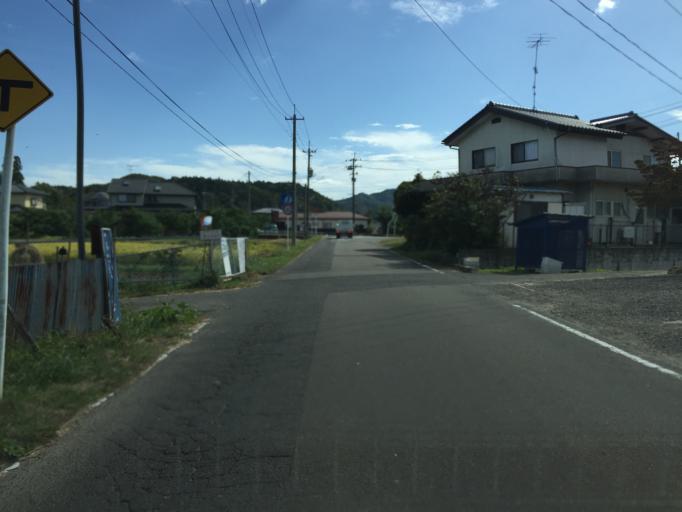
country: JP
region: Fukushima
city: Hobaramachi
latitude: 37.8066
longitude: 140.5728
